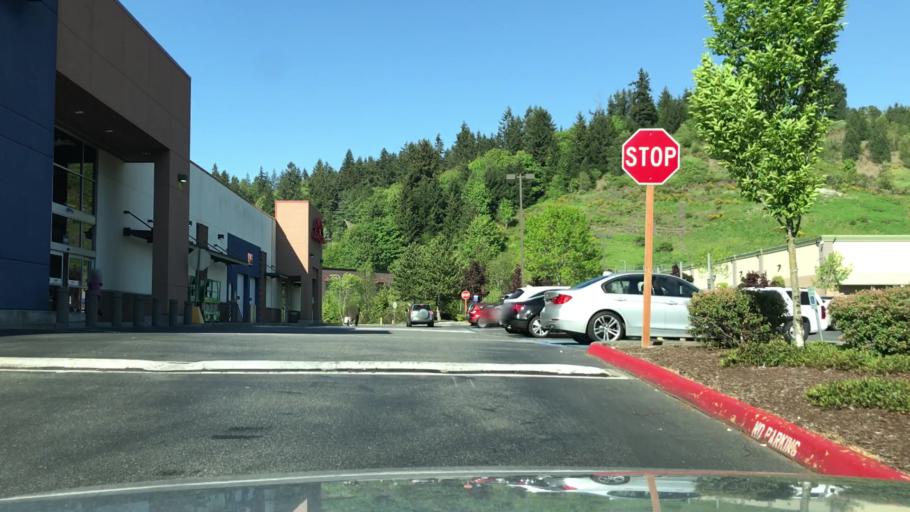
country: US
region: Washington
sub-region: King County
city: Issaquah
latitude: 47.5488
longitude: -122.0414
